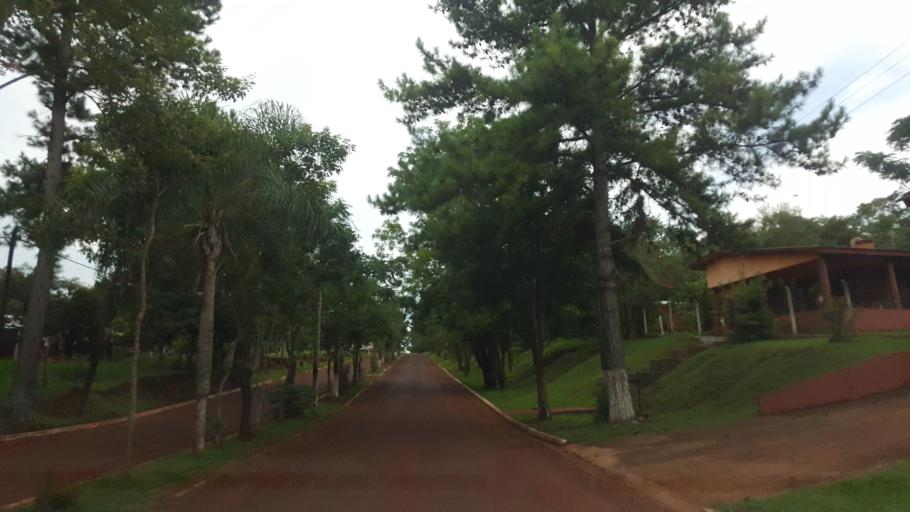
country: AR
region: Misiones
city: Santo Pipo
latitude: -27.1106
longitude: -55.3771
